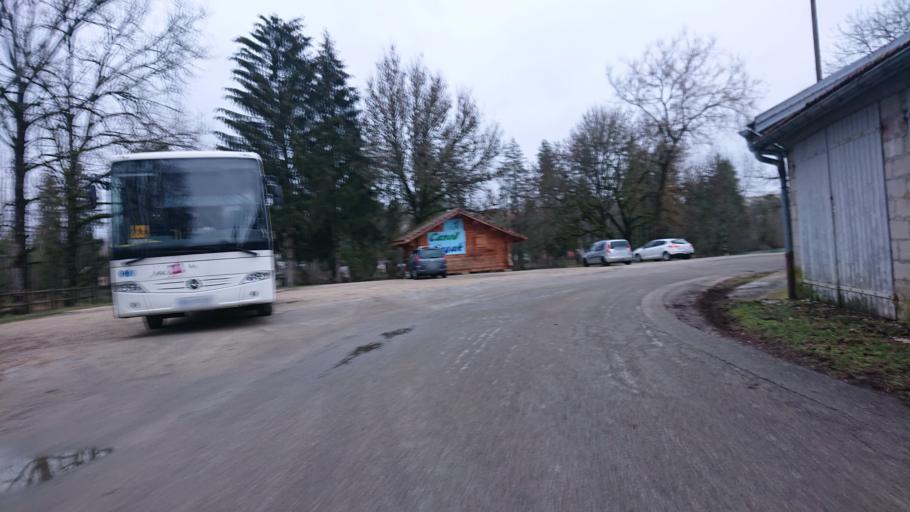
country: FR
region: Franche-Comte
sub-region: Departement du Jura
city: Clairvaux-les-Lacs
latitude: 46.5867
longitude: 5.6970
